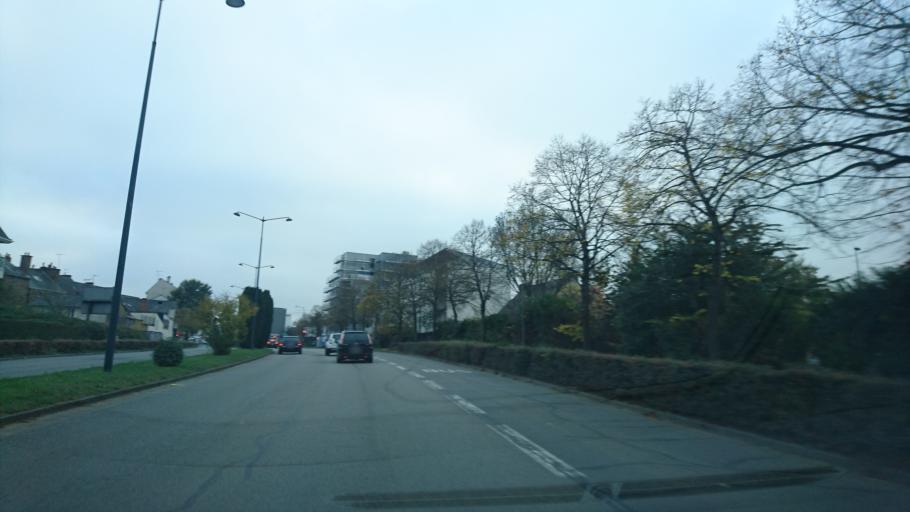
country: FR
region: Brittany
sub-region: Departement d'Ille-et-Vilaine
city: Rennes
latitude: 48.0994
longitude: -1.6875
